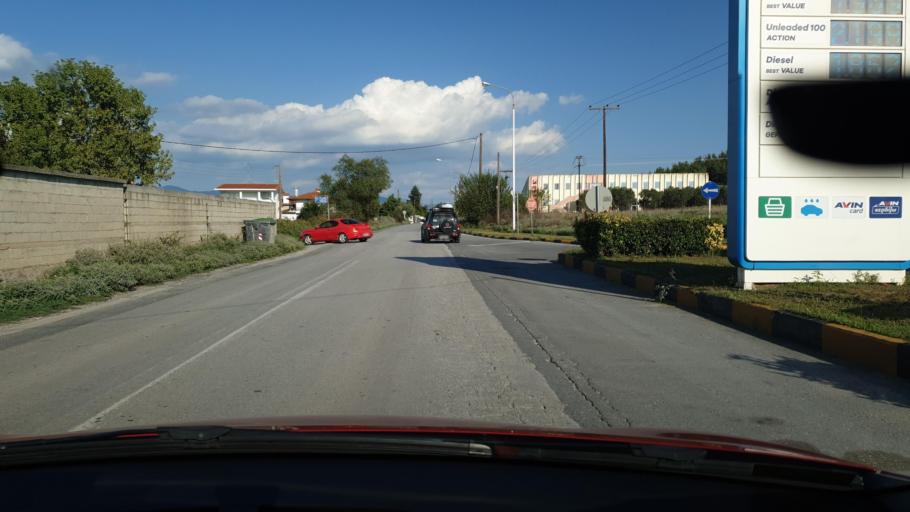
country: GR
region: Central Macedonia
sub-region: Nomos Thessalonikis
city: Neo Rysi
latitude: 40.4948
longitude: 23.0093
